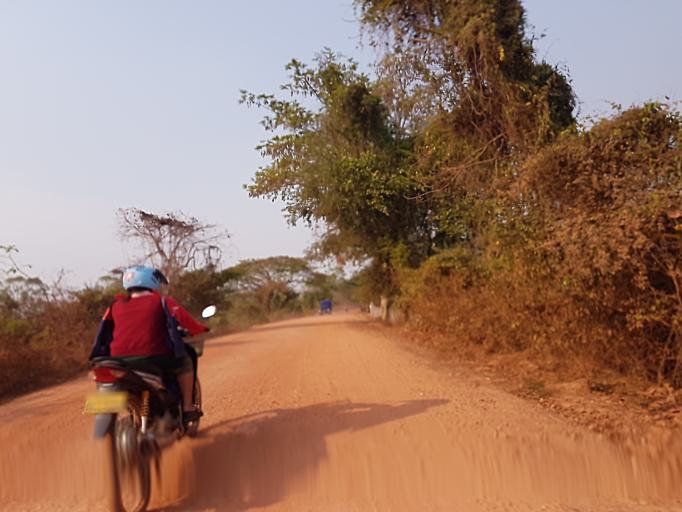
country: TH
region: Nong Khai
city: Phon Phisai
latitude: 18.0047
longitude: 102.9079
